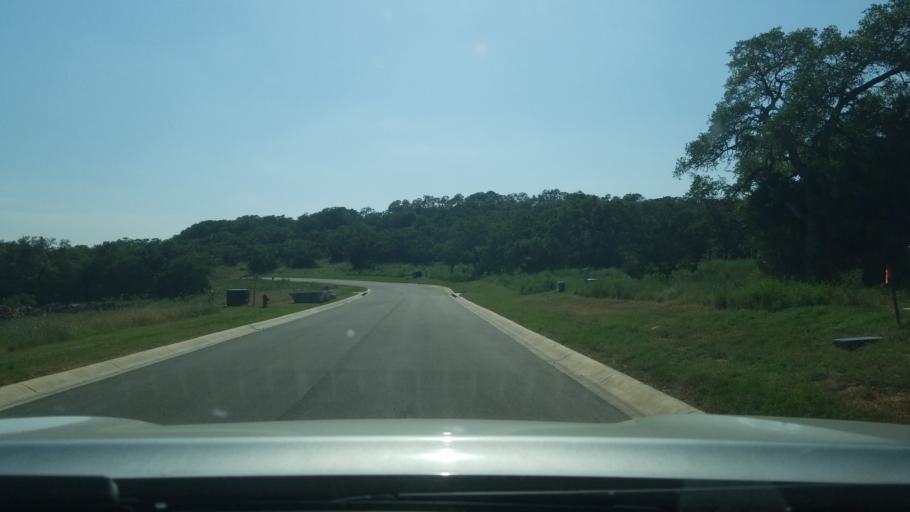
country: US
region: Texas
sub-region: Comal County
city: Bulverde
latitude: 29.7639
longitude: -98.4200
